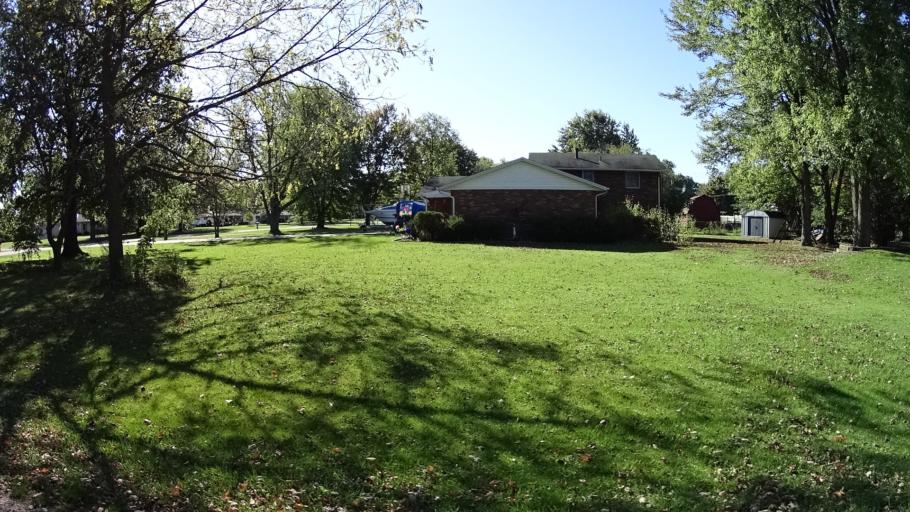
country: US
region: Ohio
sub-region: Lorain County
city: Amherst
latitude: 41.4170
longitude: -82.2128
